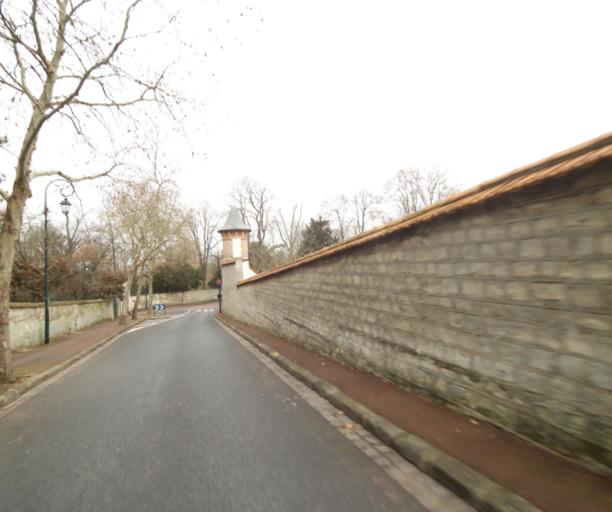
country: FR
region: Ile-de-France
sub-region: Departement des Hauts-de-Seine
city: Rueil-Malmaison
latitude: 48.8701
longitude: 2.1695
